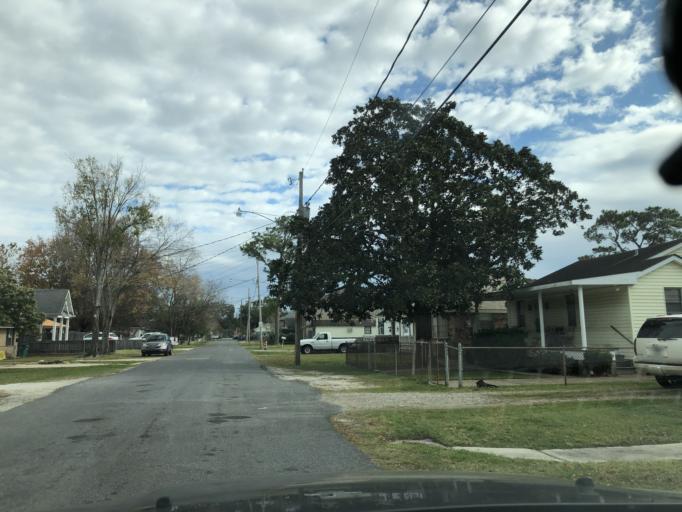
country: US
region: Louisiana
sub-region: Jefferson Parish
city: Metairie Terrace
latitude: 29.9793
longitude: -90.1690
